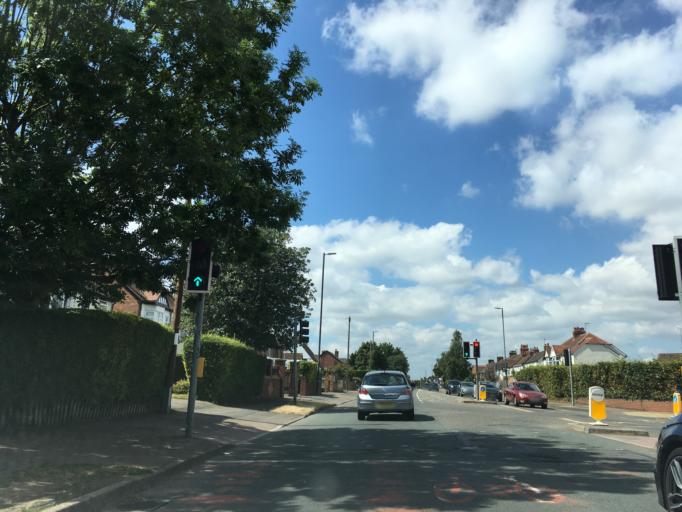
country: GB
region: England
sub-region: Gloucestershire
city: Barnwood
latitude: 51.8752
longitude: -2.2073
